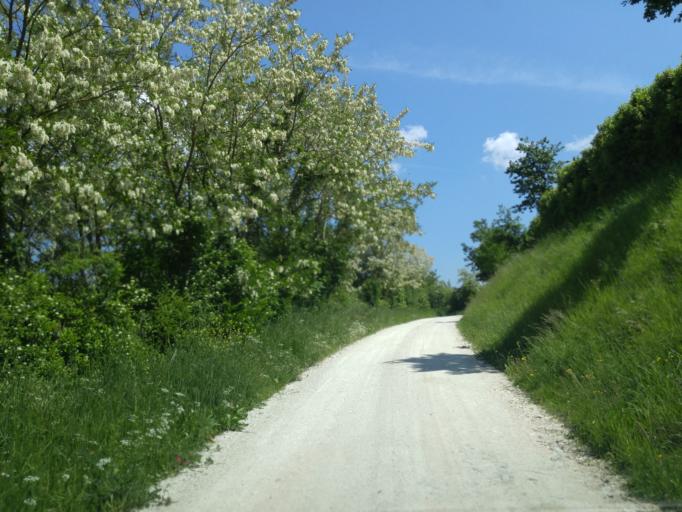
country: IT
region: The Marches
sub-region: Provincia di Pesaro e Urbino
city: Fermignano
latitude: 43.7006
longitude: 12.6510
